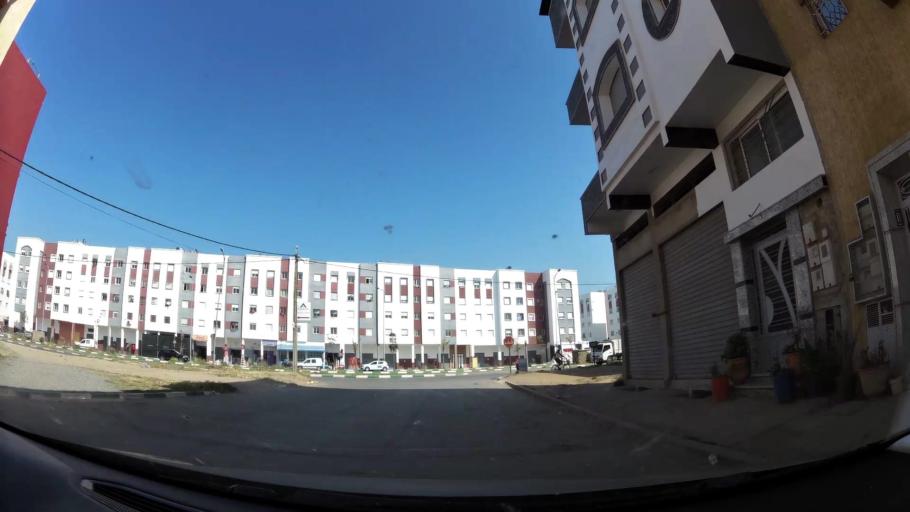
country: MA
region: Rabat-Sale-Zemmour-Zaer
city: Sale
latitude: 34.0654
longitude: -6.7635
